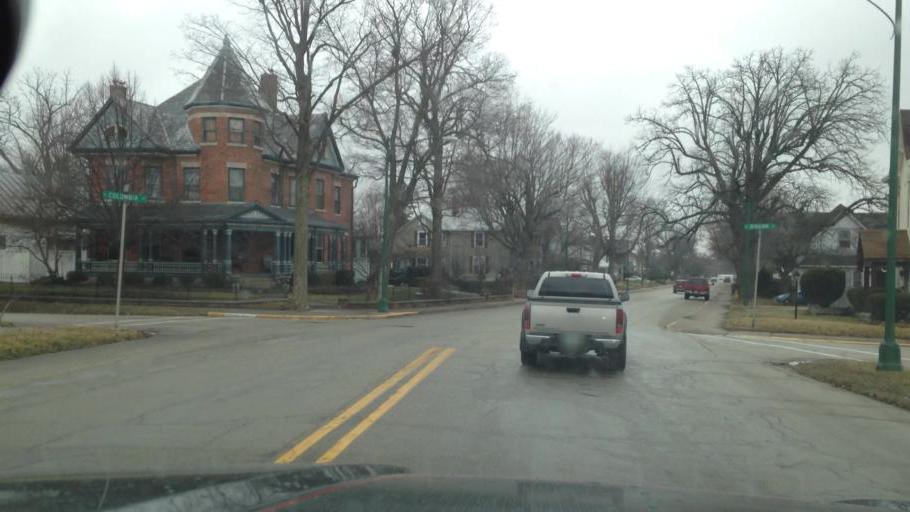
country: US
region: Indiana
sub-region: Randolph County
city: Union City
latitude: 40.2018
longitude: -84.8090
